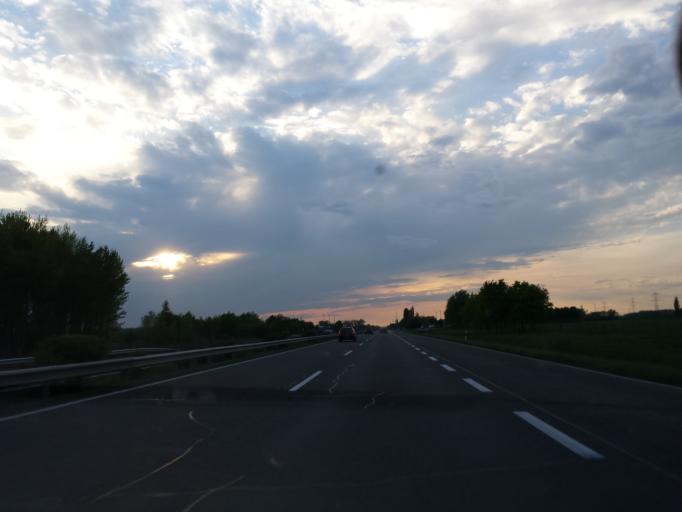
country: HU
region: Gyor-Moson-Sopron
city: Lebeny
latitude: 47.7631
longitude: 17.3920
